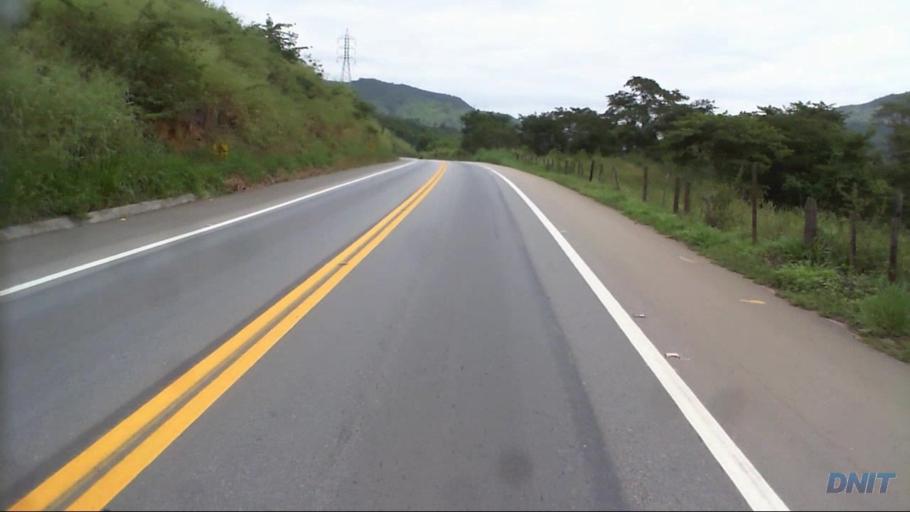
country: BR
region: Minas Gerais
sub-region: Timoteo
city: Timoteo
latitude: -19.5884
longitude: -42.7342
